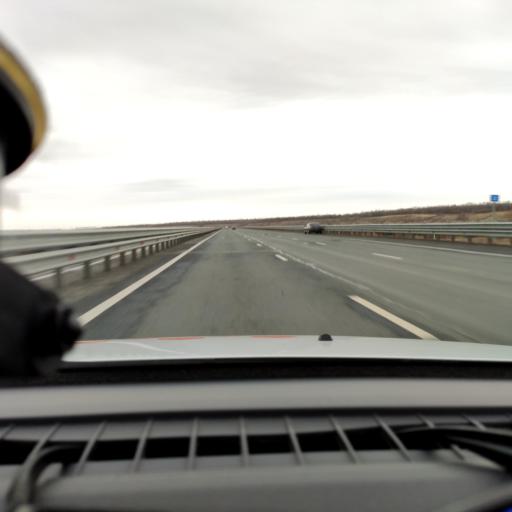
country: RU
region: Samara
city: Smyshlyayevka
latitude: 53.1537
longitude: 50.3477
